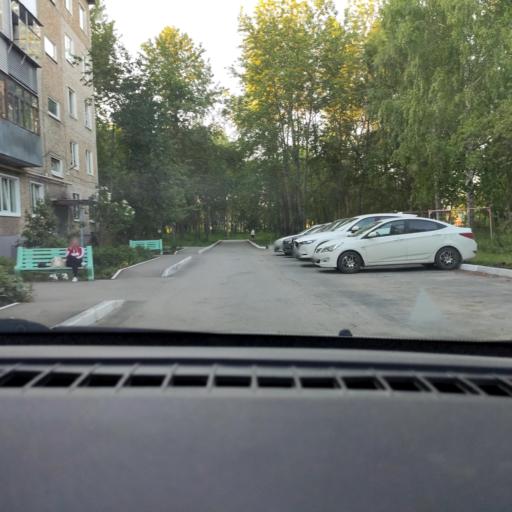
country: RU
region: Perm
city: Polazna
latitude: 58.1464
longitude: 56.4424
